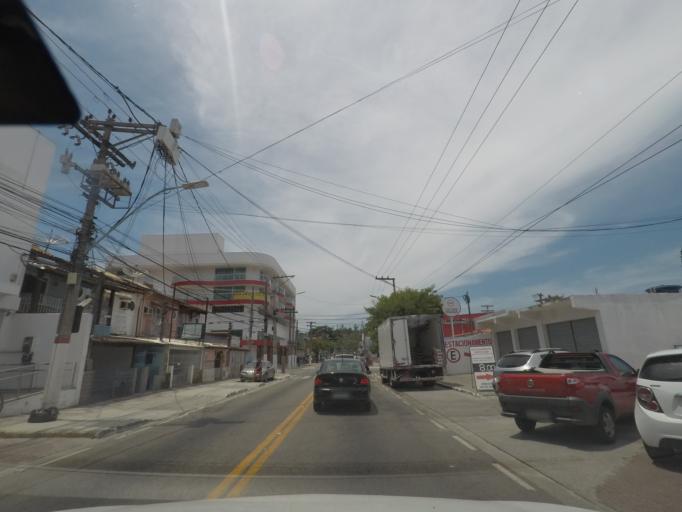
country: BR
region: Rio de Janeiro
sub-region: Marica
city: Marica
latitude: -22.9206
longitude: -42.8178
